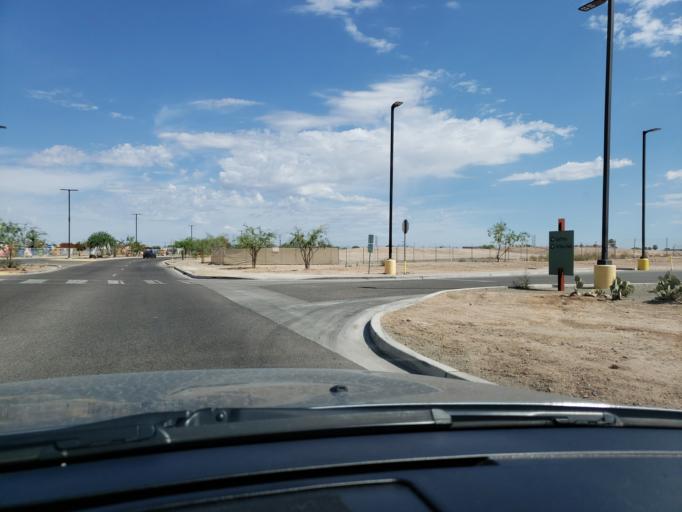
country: US
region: Arizona
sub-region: Maricopa County
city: Peoria
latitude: 33.5473
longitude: -112.2592
